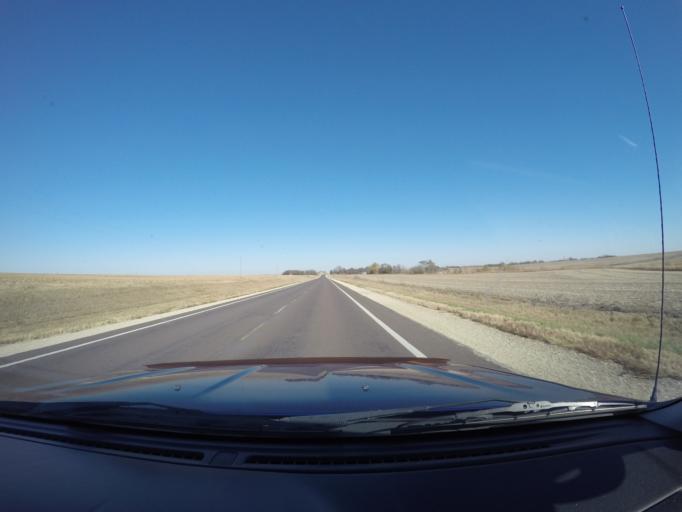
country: US
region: Kansas
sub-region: Marshall County
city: Blue Rapids
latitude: 39.6192
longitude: -96.7502
